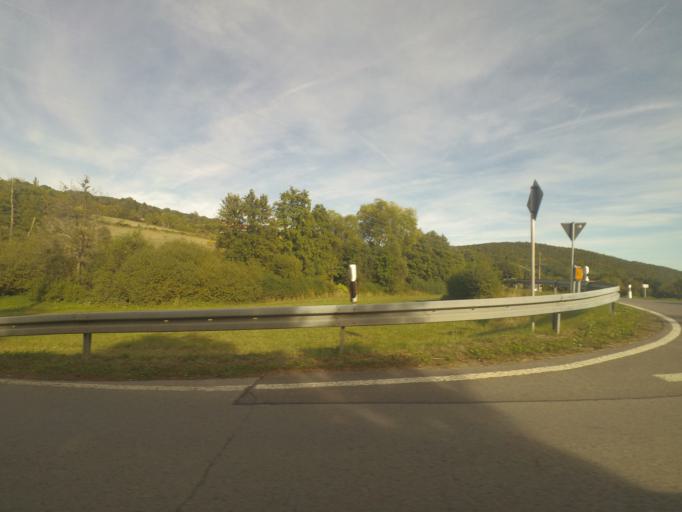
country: DE
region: Bavaria
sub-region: Regierungsbezirk Unterfranken
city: Fladungen
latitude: 50.5242
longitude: 10.1471
